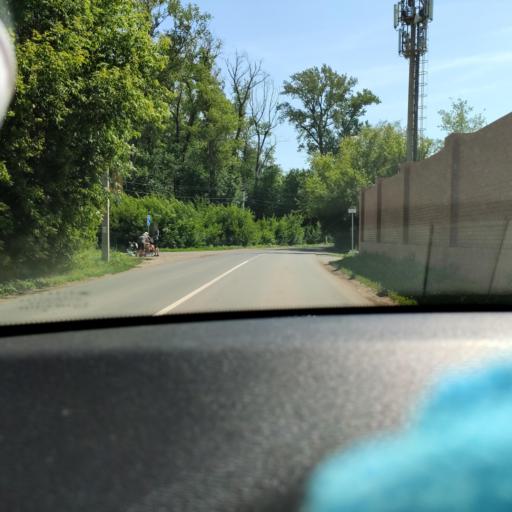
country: RU
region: Samara
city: Novokuybyshevsk
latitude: 53.1605
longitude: 49.9481
